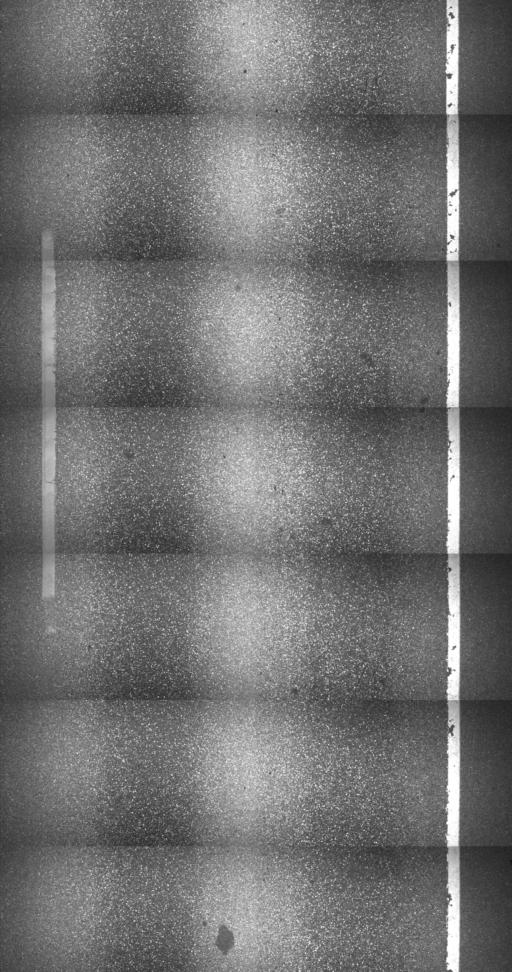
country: US
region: Vermont
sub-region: Chittenden County
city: Hinesburg
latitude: 44.2809
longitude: -73.0686
